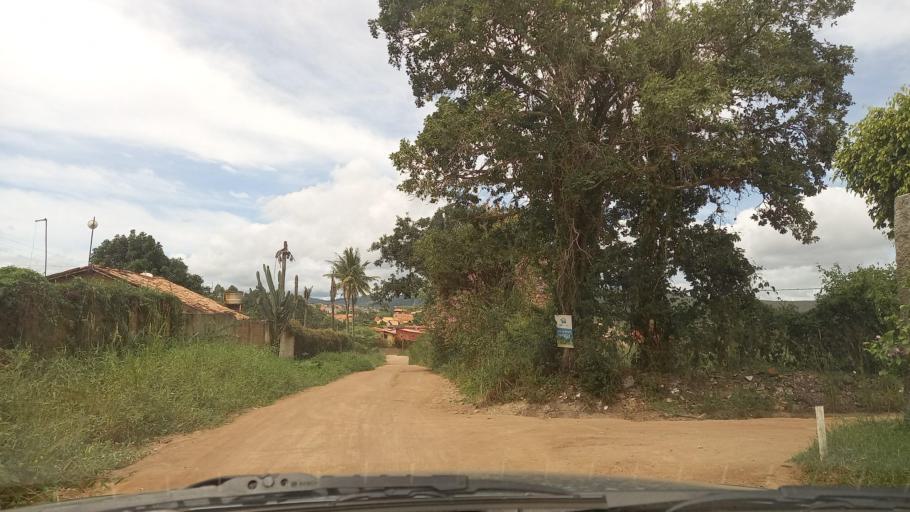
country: BR
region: Pernambuco
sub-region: Gravata
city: Gravata
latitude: -8.1934
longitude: -35.5895
